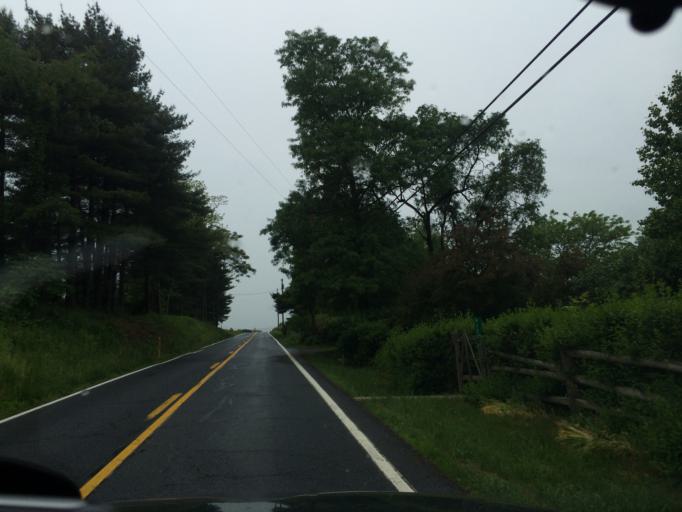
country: US
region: Maryland
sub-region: Frederick County
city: Thurmont
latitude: 39.6117
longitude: -77.3473
